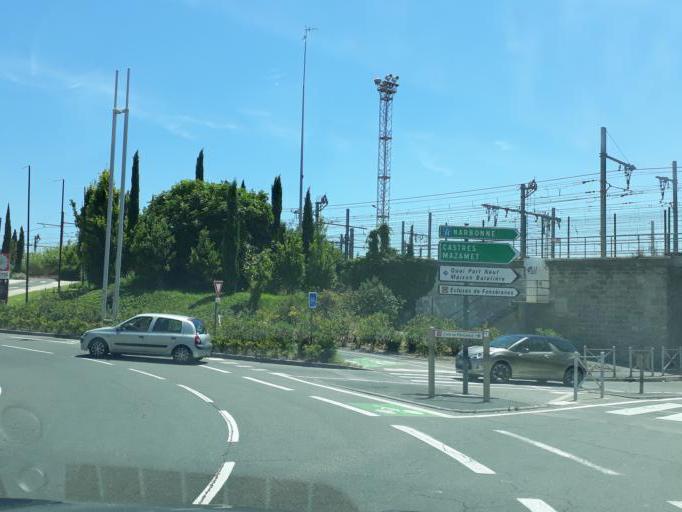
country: FR
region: Languedoc-Roussillon
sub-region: Departement de l'Herault
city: Beziers
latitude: 43.3361
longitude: 3.2225
